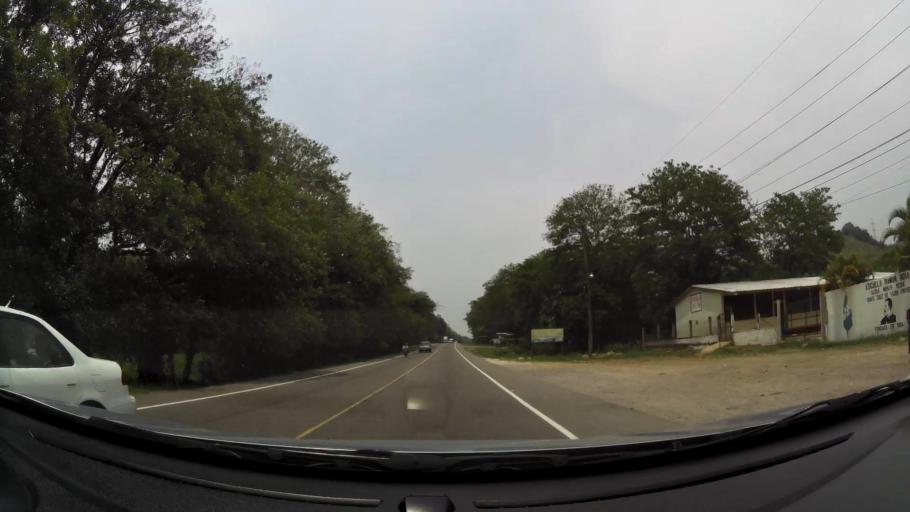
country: HN
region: Cortes
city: La Guama
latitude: 14.8644
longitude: -87.9504
